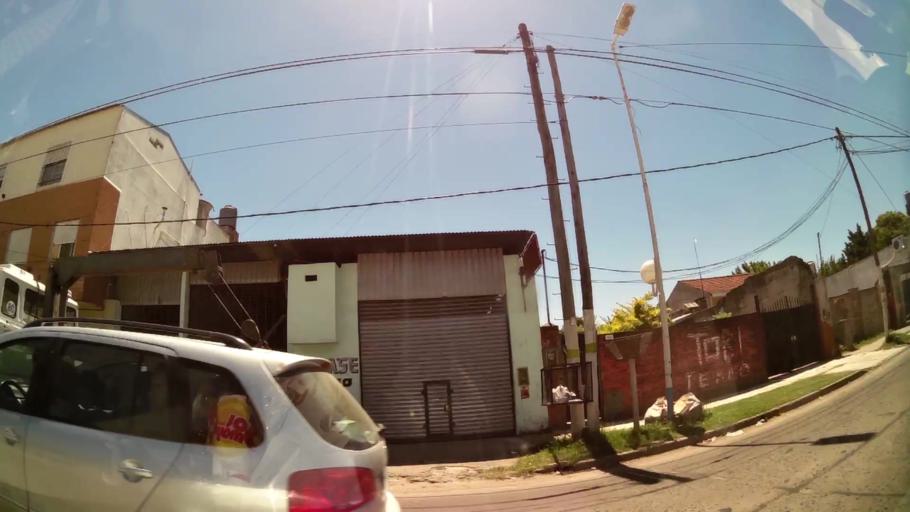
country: AR
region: Buenos Aires
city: Hurlingham
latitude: -34.5025
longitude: -58.6818
